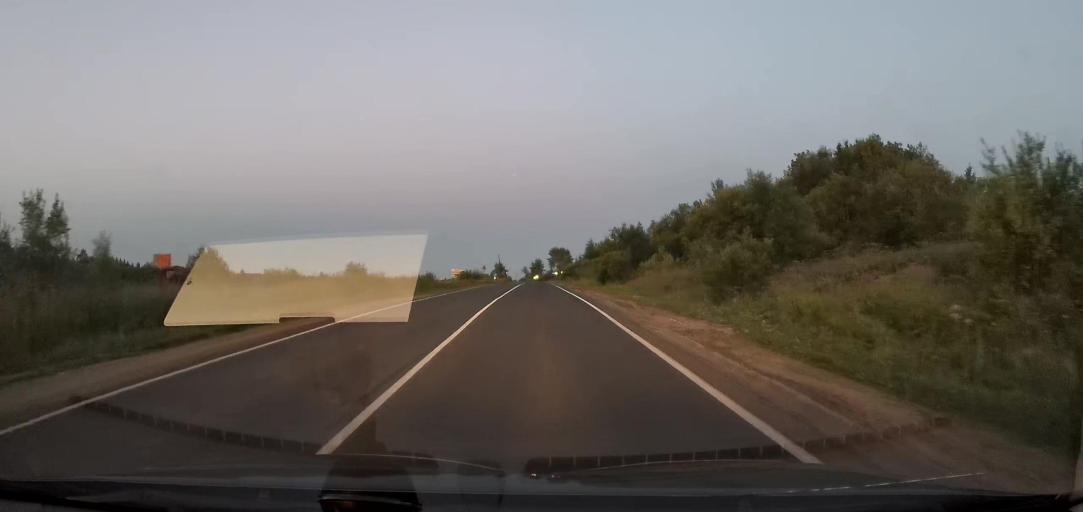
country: RU
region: Arkhangelskaya
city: Uyemskiy
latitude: 64.4489
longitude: 40.9450
